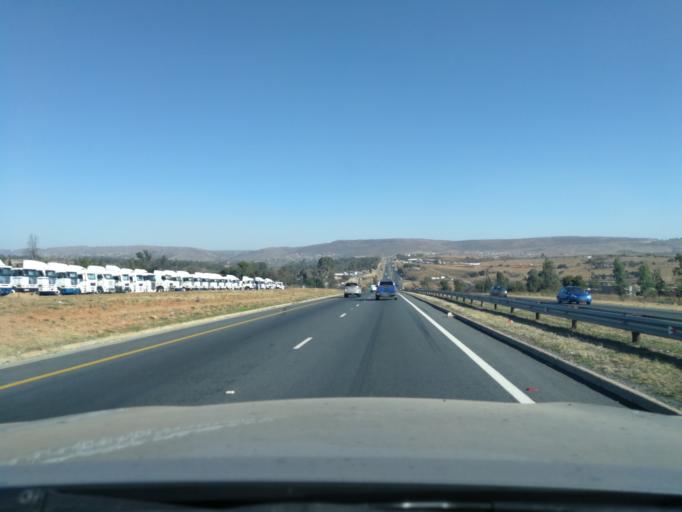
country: ZA
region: Gauteng
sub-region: West Rand District Municipality
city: Muldersdriseloop
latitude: -26.0310
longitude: 27.8485
